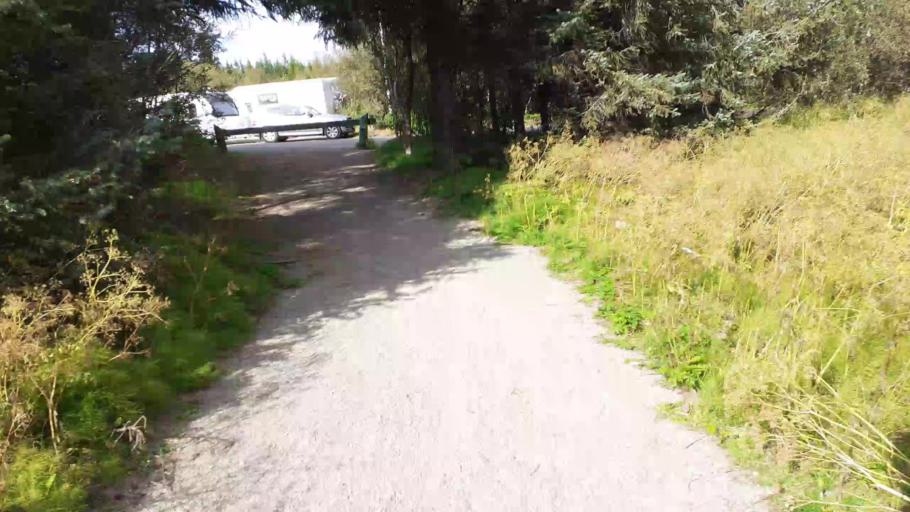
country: IS
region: Northeast
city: Akureyri
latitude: 65.6462
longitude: -18.0859
